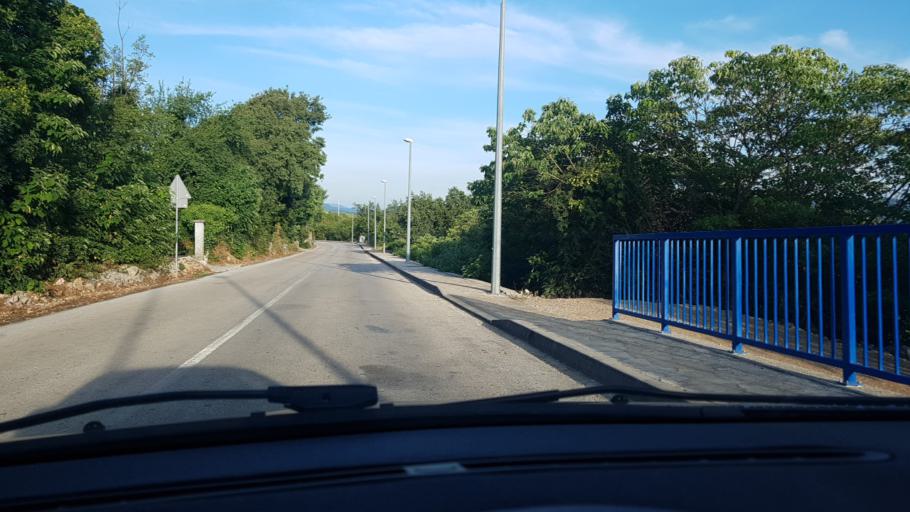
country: HR
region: Splitsko-Dalmatinska
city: Imotski
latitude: 43.4452
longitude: 17.2021
